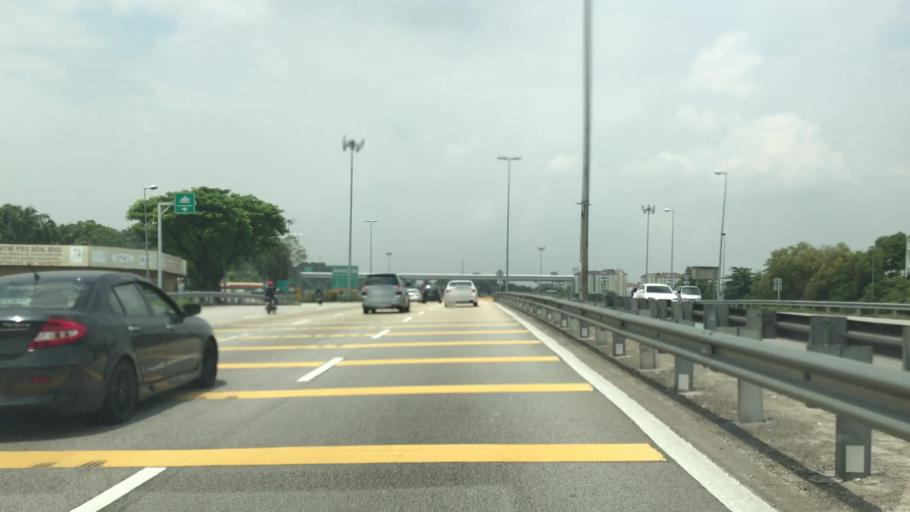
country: MY
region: Putrajaya
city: Putrajaya
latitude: 2.9835
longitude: 101.6336
